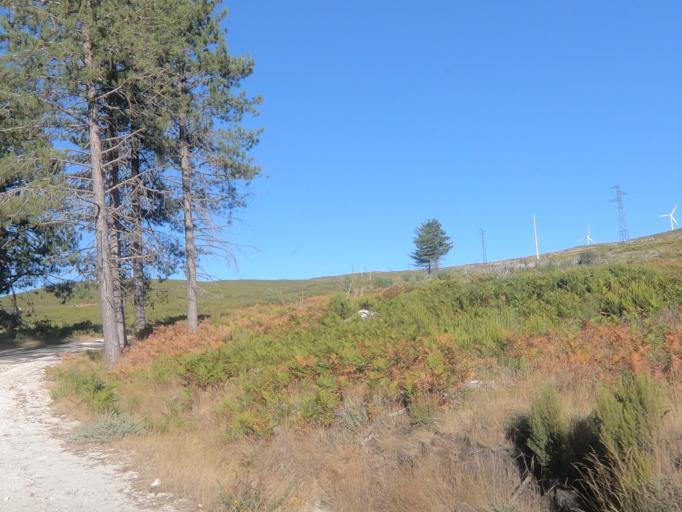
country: PT
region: Vila Real
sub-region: Vila Real
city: Vila Real
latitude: 41.3550
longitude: -7.7864
